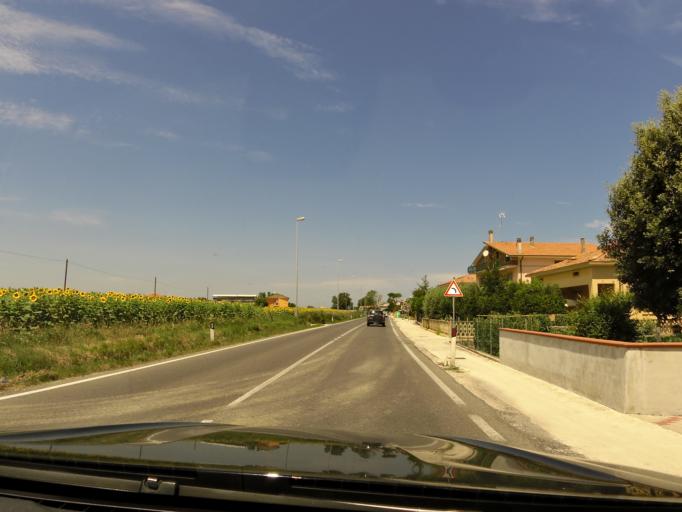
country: IT
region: The Marches
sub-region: Provincia di Pesaro e Urbino
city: Marotta
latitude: 43.7886
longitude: 13.1075
